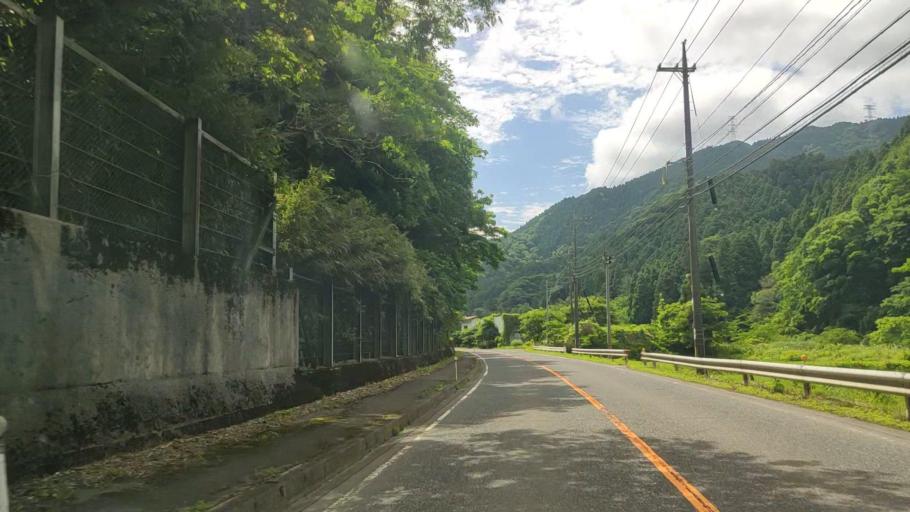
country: JP
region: Okayama
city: Niimi
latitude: 35.2190
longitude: 133.4531
